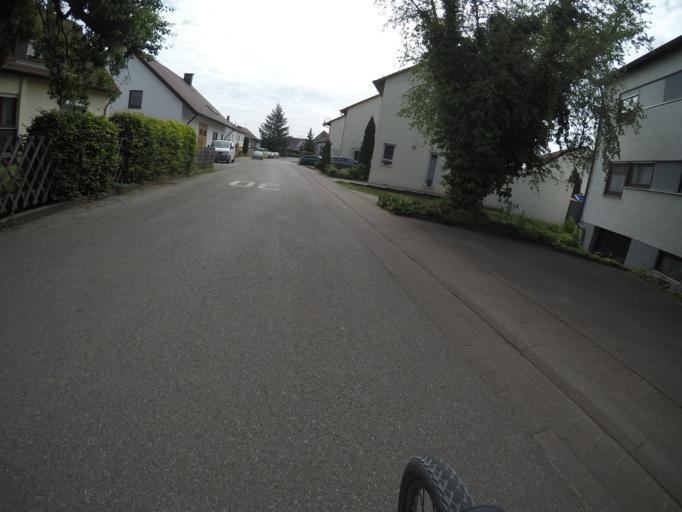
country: DE
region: Baden-Wuerttemberg
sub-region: Regierungsbezirk Stuttgart
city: Wendlingen am Neckar
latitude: 48.6457
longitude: 9.4103
